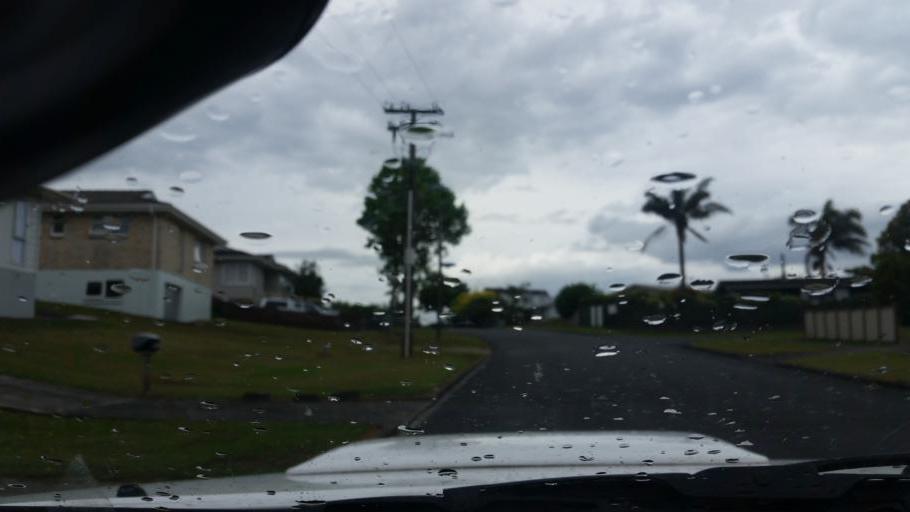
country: NZ
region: Northland
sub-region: Kaipara District
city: Dargaville
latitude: -35.9293
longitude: 173.8637
